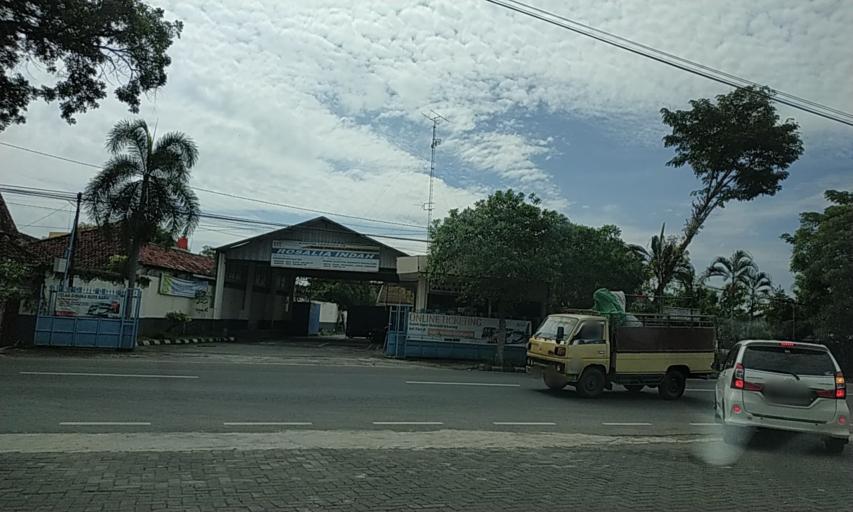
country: ID
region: Central Java
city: Selogiri
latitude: -7.7961
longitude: 110.9060
